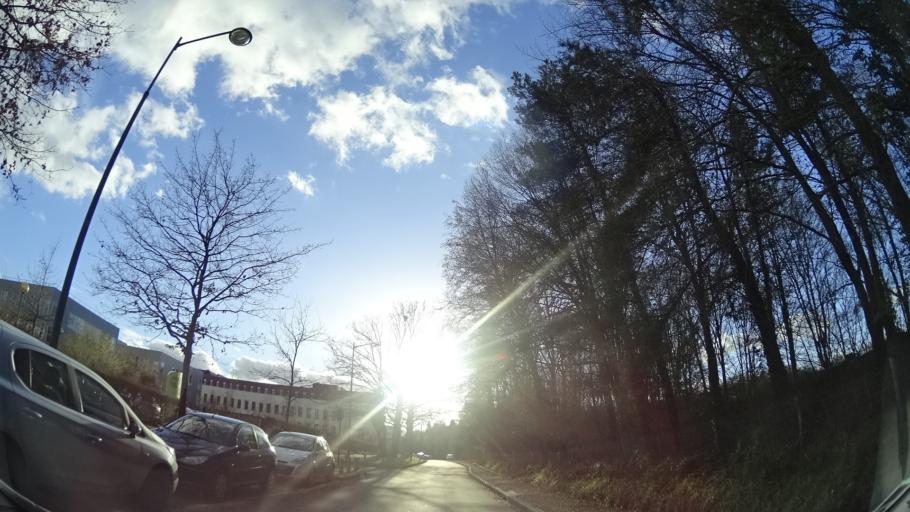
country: FR
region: Brittany
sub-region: Departement d'Ille-et-Vilaine
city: Cesson-Sevigne
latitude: 48.1319
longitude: -1.6403
